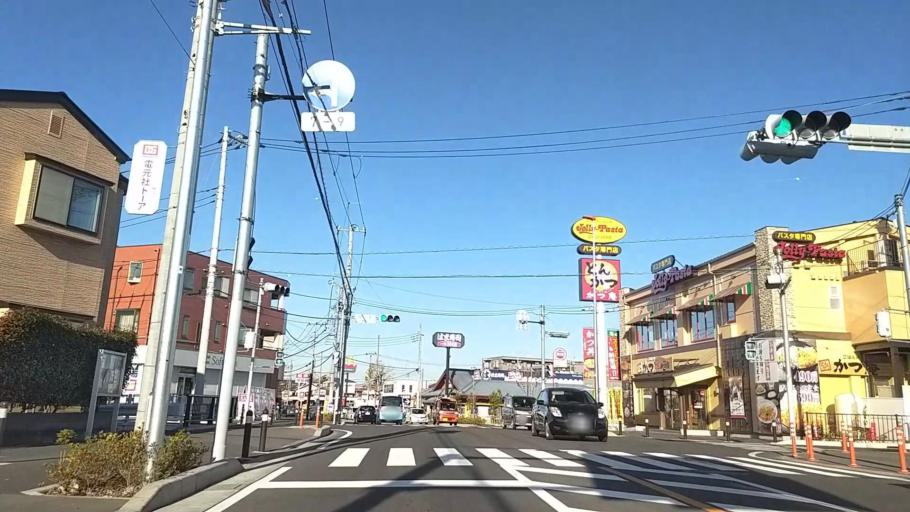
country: JP
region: Tokyo
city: Chofugaoka
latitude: 35.6211
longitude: 139.5516
